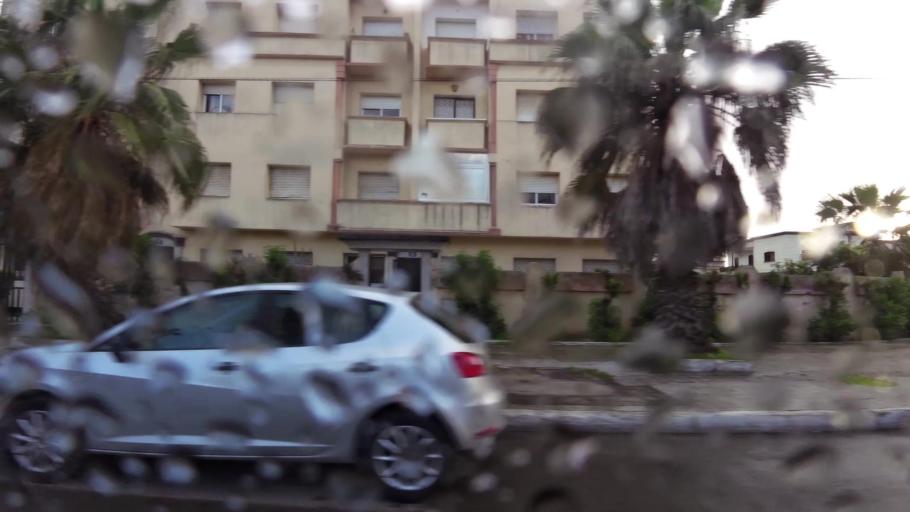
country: MA
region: Doukkala-Abda
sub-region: El-Jadida
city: El Jadida
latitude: 33.2296
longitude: -8.4973
